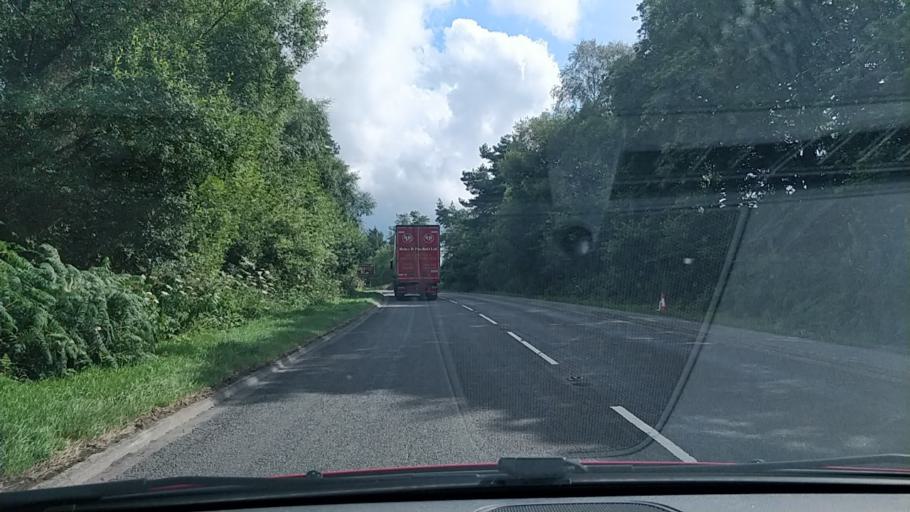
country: GB
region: Wales
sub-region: Gwynedd
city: Trawsfynydd
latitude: 52.9101
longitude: -3.9245
